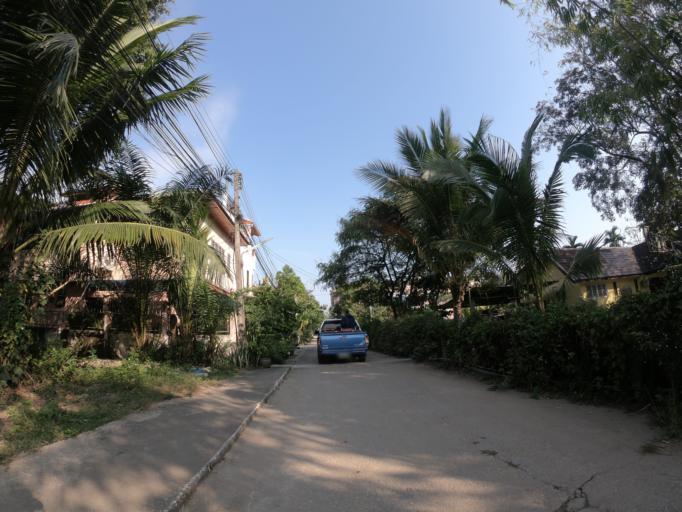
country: TH
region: Chiang Mai
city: Chiang Mai
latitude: 18.8026
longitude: 99.0094
